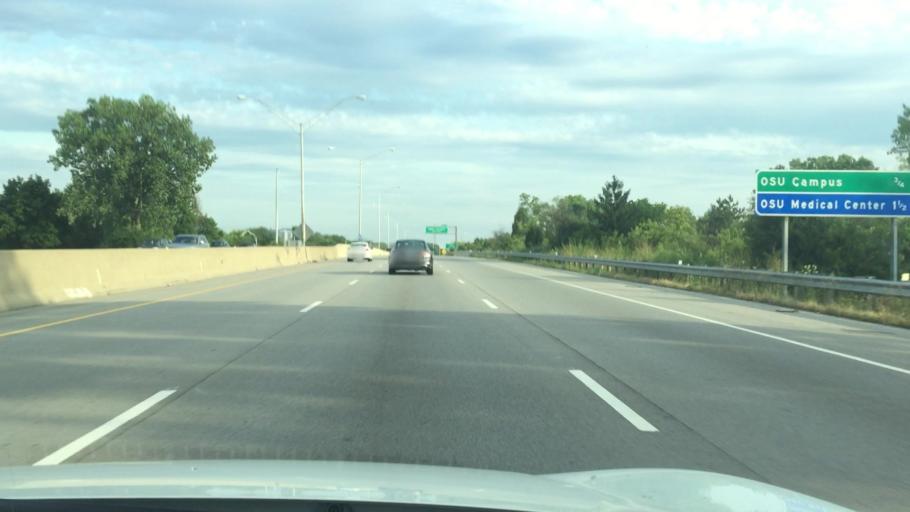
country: US
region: Ohio
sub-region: Franklin County
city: Upper Arlington
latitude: 40.0201
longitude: -83.0349
